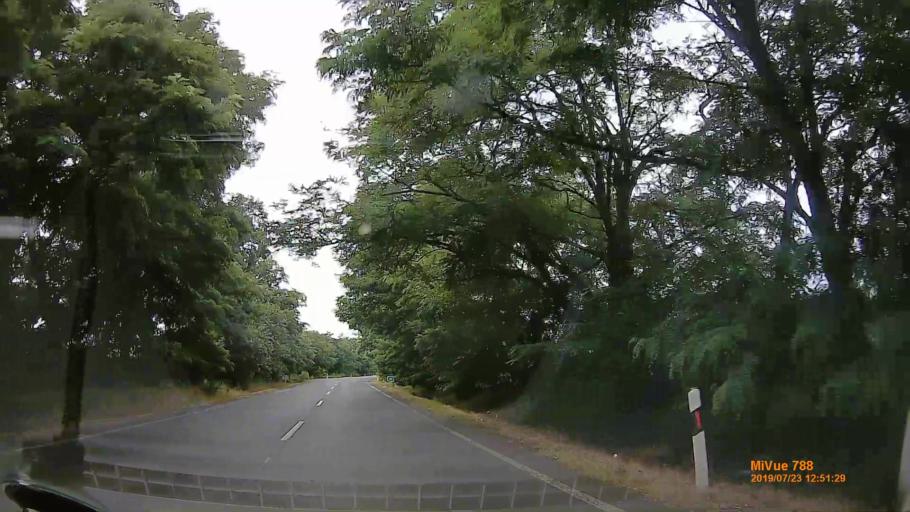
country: HU
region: Szabolcs-Szatmar-Bereg
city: Nagycserkesz
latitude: 47.9592
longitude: 21.5859
